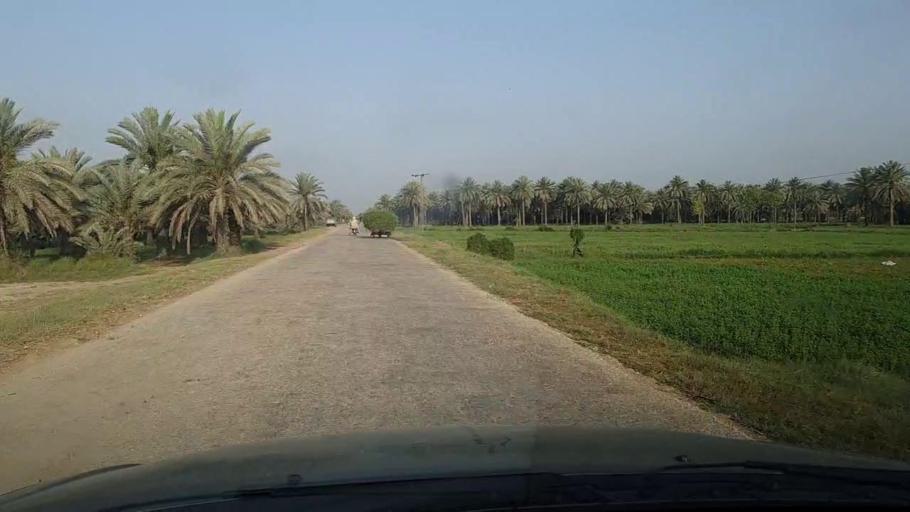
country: PK
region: Sindh
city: Pir jo Goth
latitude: 27.5634
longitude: 68.6542
